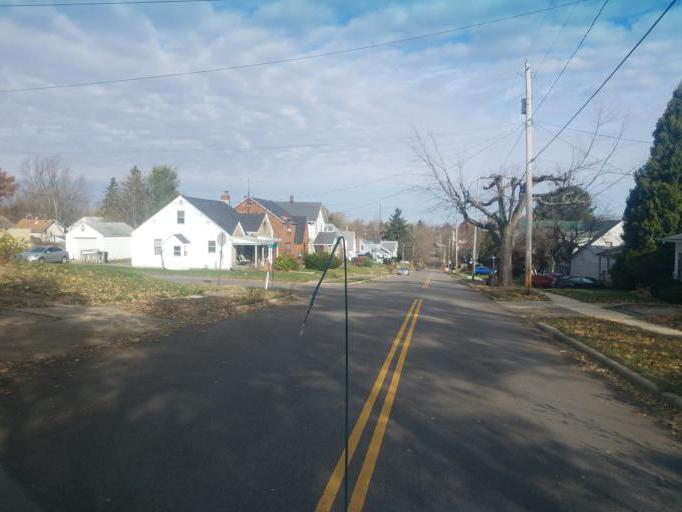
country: US
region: Ohio
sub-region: Richland County
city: Mansfield
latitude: 40.7485
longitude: -82.5230
